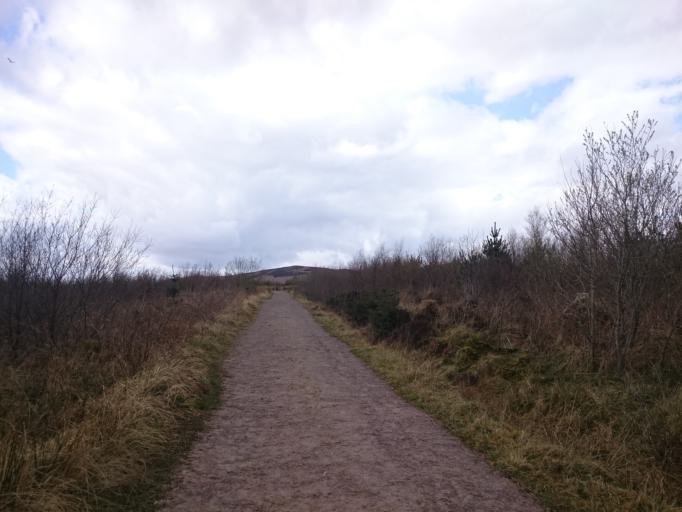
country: GB
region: Scotland
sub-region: Stirling
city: Killearn
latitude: 56.0924
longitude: -4.4869
